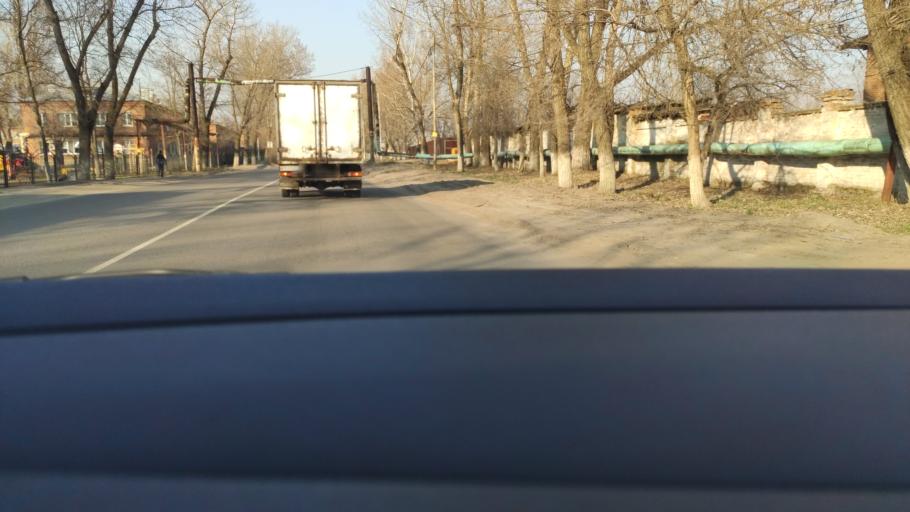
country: RU
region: Voronezj
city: Maslovka
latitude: 51.5812
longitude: 39.3162
